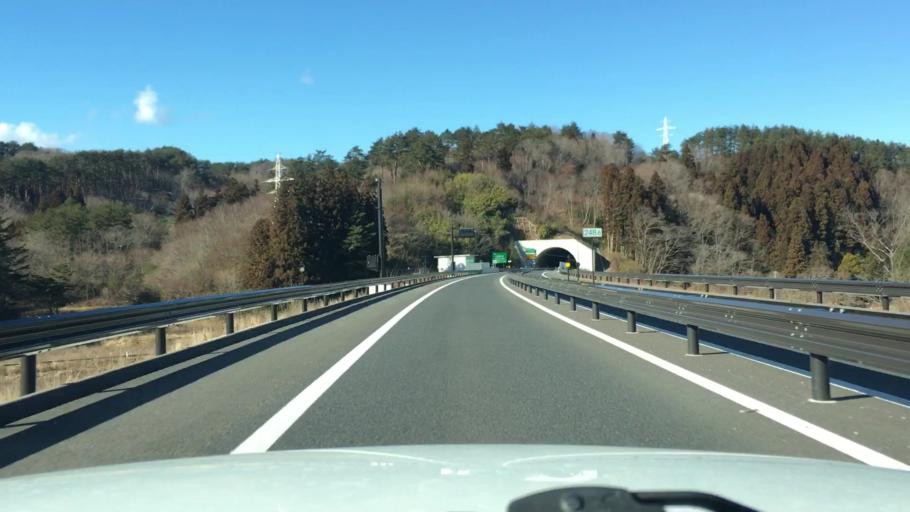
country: JP
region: Iwate
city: Yamada
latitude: 39.5272
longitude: 141.9228
